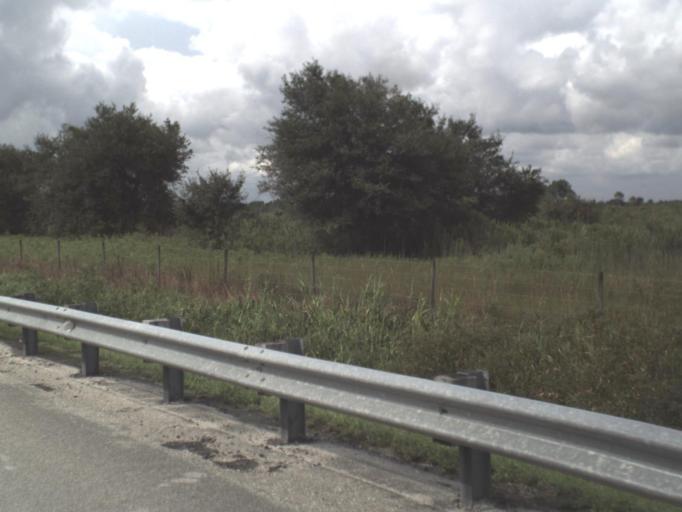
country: US
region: Florida
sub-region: Sarasota County
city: Warm Mineral Springs
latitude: 27.1946
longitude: -82.1995
